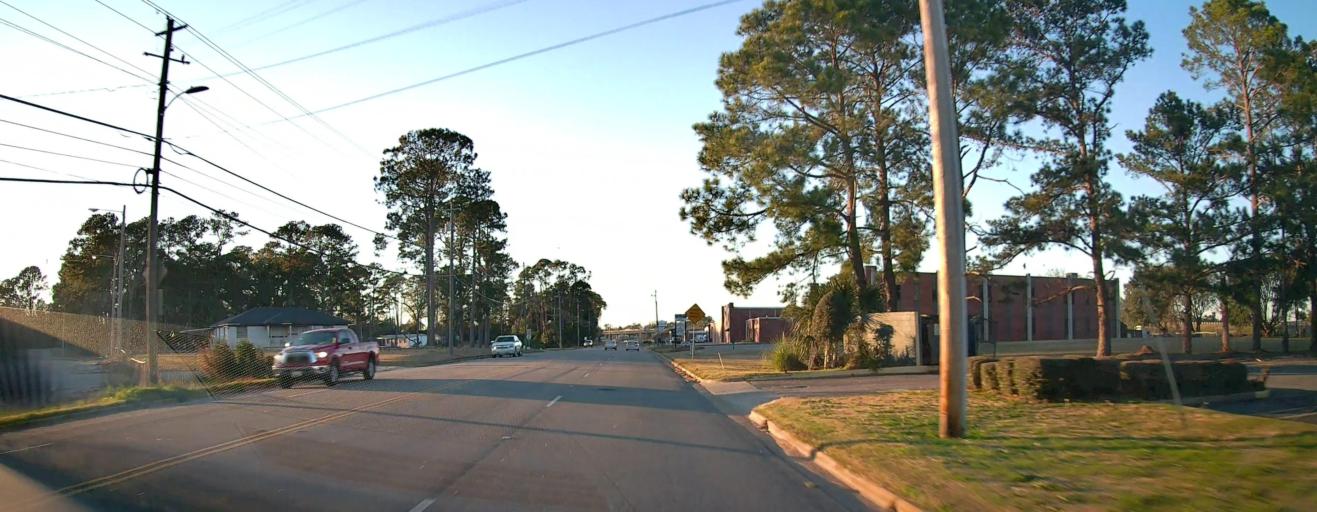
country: US
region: Georgia
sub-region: Dougherty County
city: Albany
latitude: 31.6130
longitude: -84.1781
